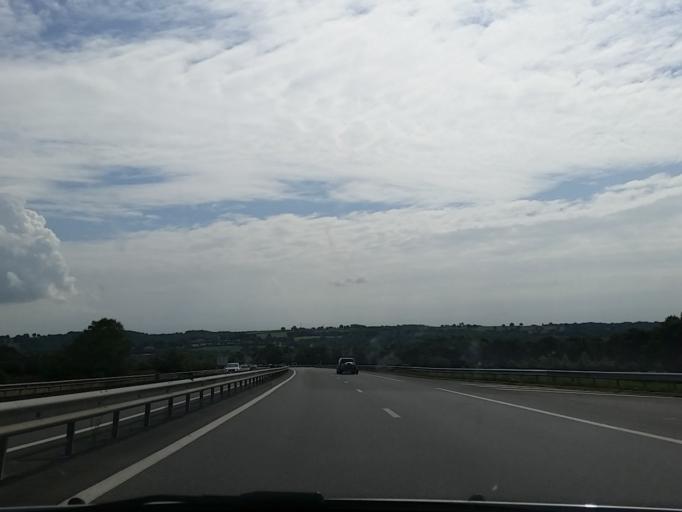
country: FR
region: Auvergne
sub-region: Departement de l'Allier
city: Vallon-en-Sully
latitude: 46.5097
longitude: 2.6054
